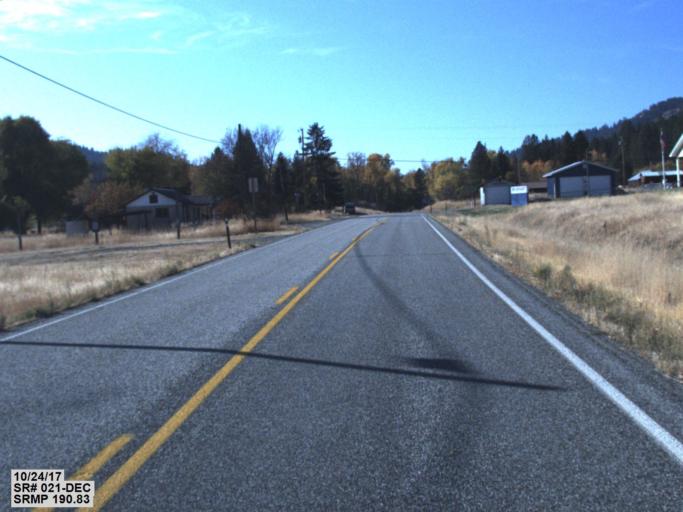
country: CA
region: British Columbia
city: Grand Forks
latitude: 48.9930
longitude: -118.5073
